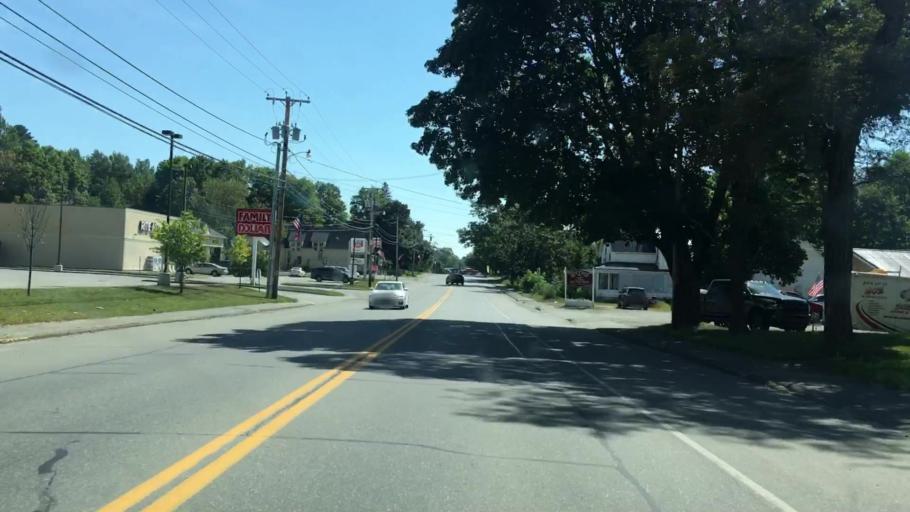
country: US
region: Maine
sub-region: Piscataquis County
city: Milo
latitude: 45.2570
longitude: -68.9872
